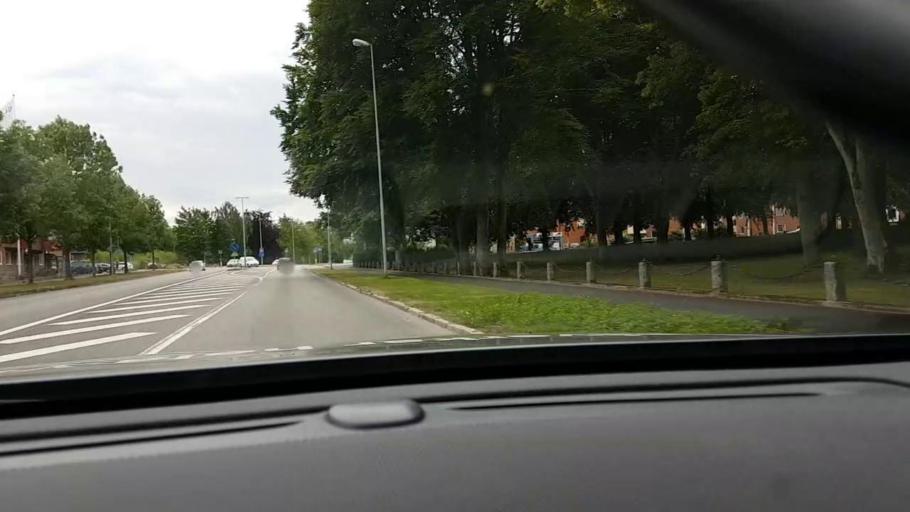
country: SE
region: Skane
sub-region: Hassleholms Kommun
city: Hassleholm
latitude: 56.1656
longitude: 13.7581
